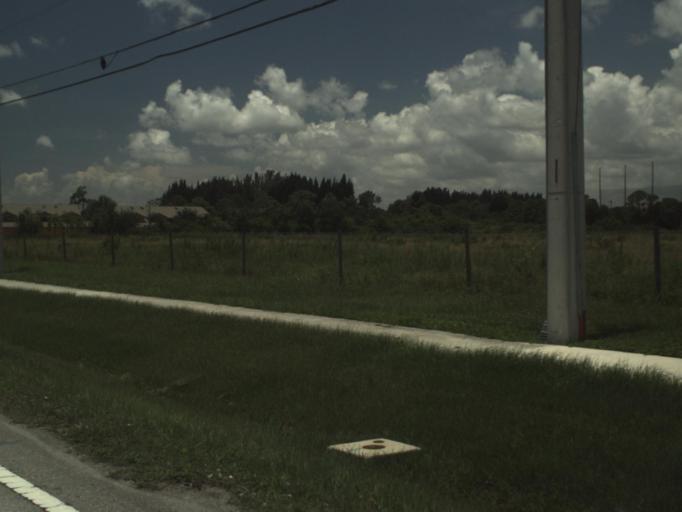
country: US
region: Florida
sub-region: Martin County
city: Palm City
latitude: 27.1176
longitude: -80.2487
